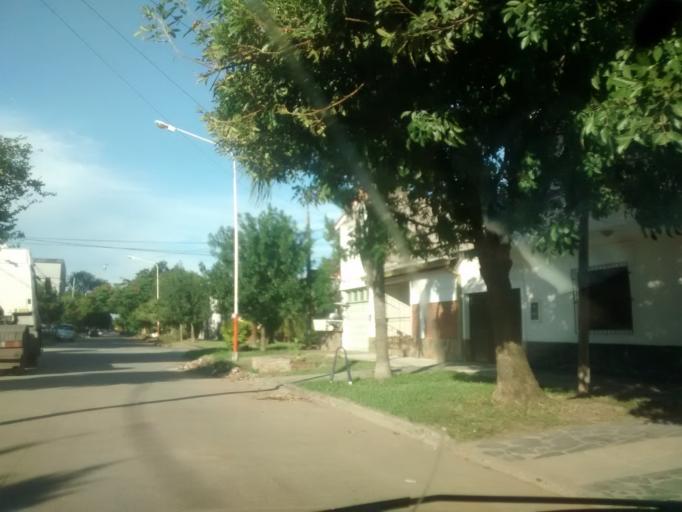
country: AR
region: Chaco
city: Resistencia
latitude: -27.4402
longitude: -59.0048
